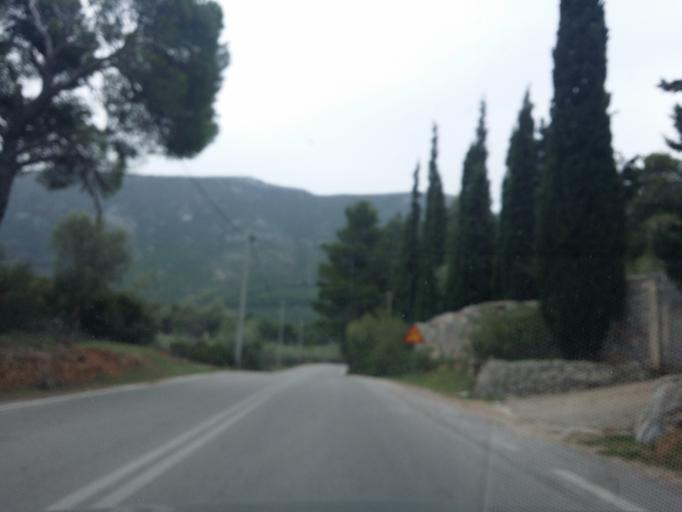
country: GR
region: Central Greece
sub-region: Nomos Voiotias
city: Kaparellion
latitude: 38.1518
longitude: 23.2459
